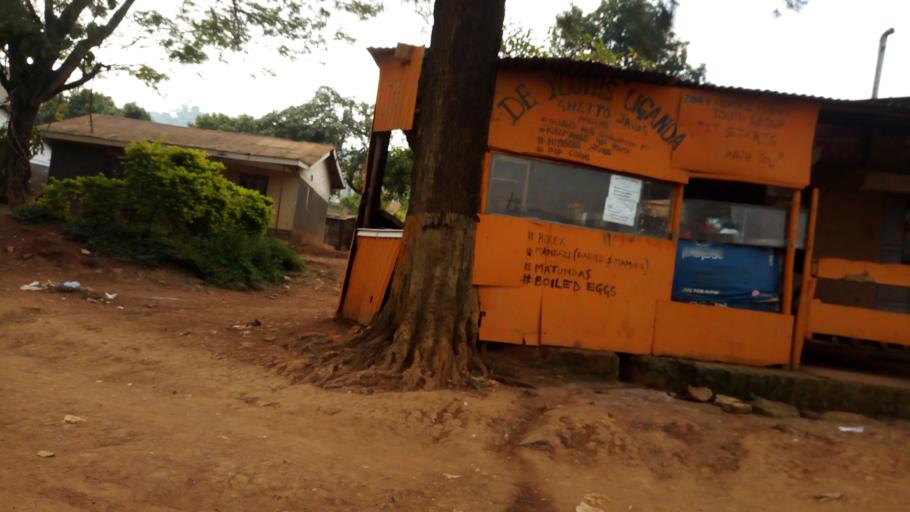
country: UG
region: Central Region
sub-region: Wakiso District
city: Kireka
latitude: 0.3213
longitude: 32.6344
